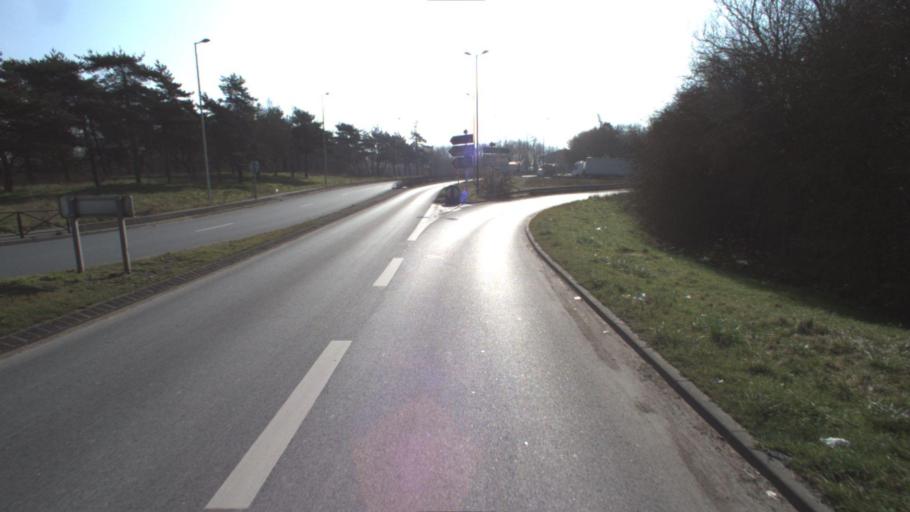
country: FR
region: Ile-de-France
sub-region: Departement de l'Essonne
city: Bondoufle
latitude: 48.6251
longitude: 2.3887
